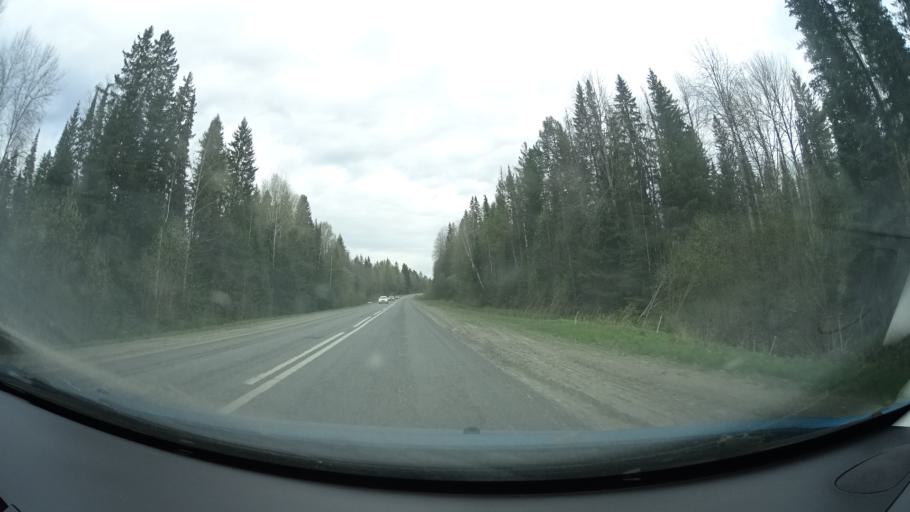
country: RU
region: Perm
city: Yugo-Kamskiy
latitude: 57.6649
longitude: 55.5919
